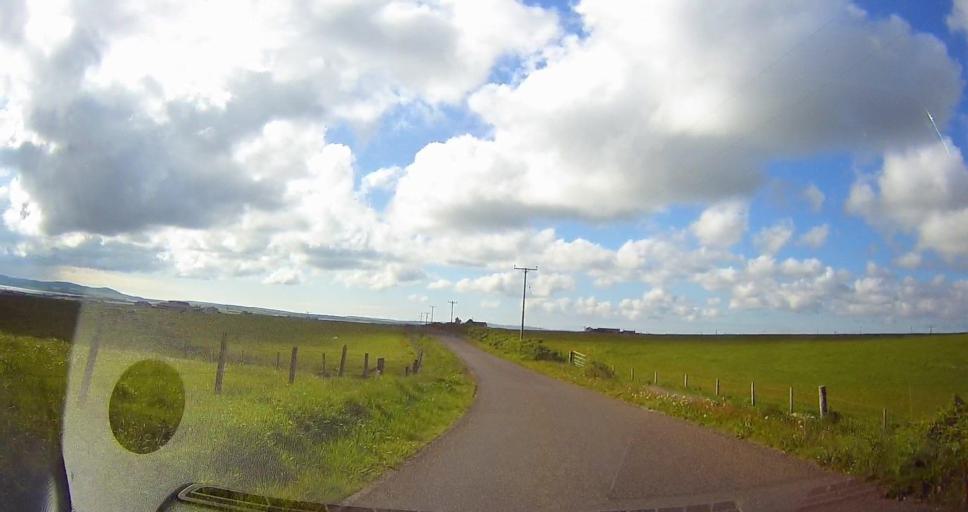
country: GB
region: Scotland
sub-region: Orkney Islands
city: Stromness
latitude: 58.9946
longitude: -3.1591
